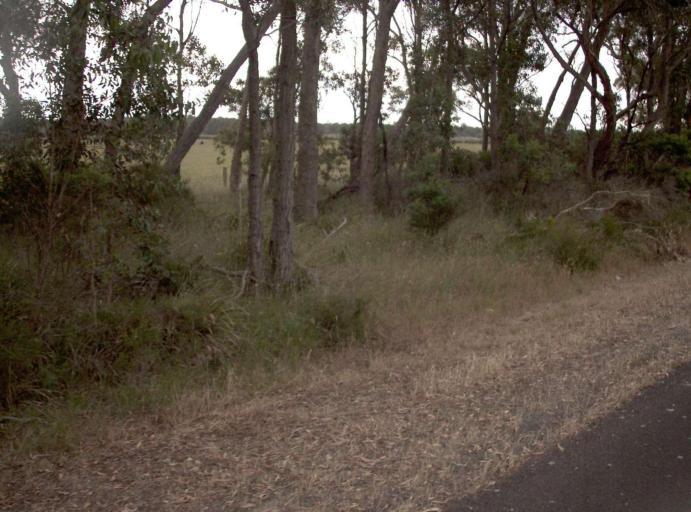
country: AU
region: Victoria
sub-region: Wellington
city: Sale
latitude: -38.4830
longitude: 146.9170
